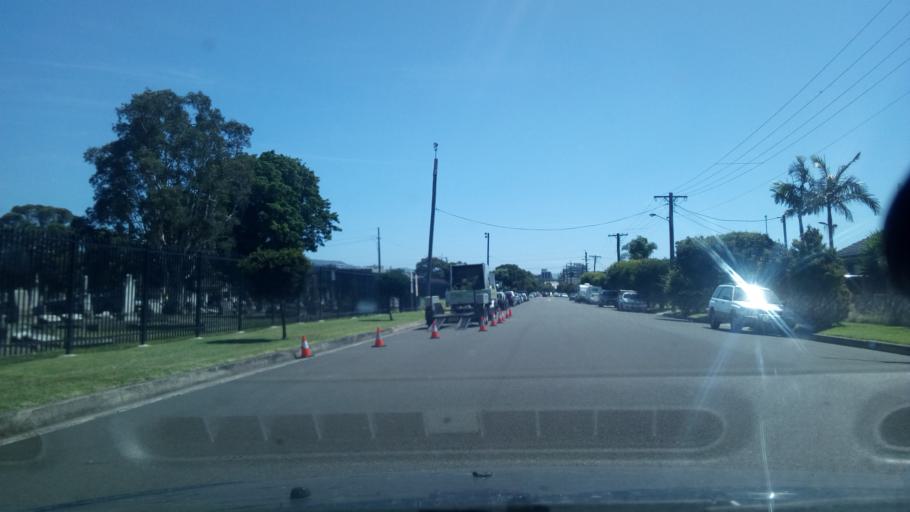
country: AU
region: New South Wales
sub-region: Wollongong
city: Wollongong
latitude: -34.4367
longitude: 150.8905
